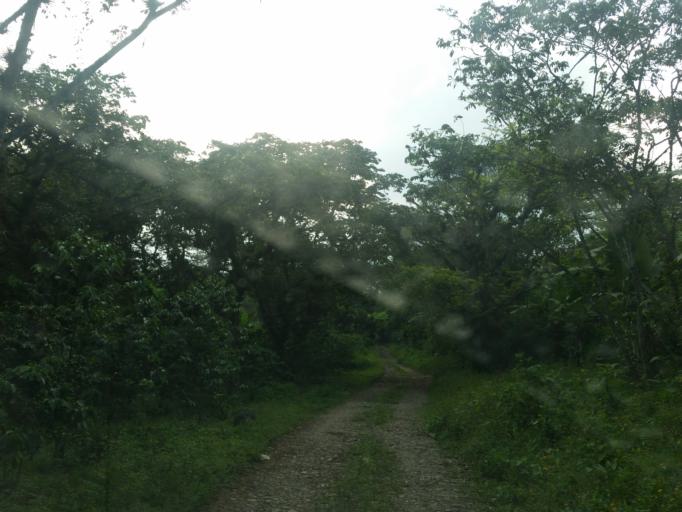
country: MX
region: Veracruz
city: Coatepec
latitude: 19.4285
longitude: -96.9586
